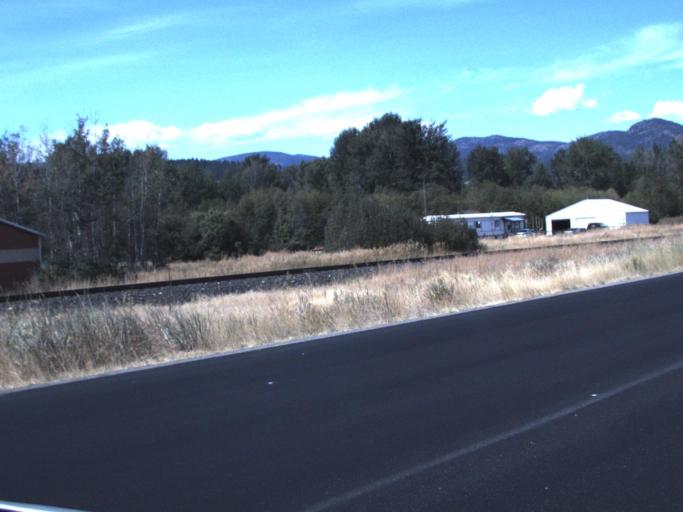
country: US
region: Washington
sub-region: Stevens County
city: Colville
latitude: 48.4635
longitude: -117.8844
